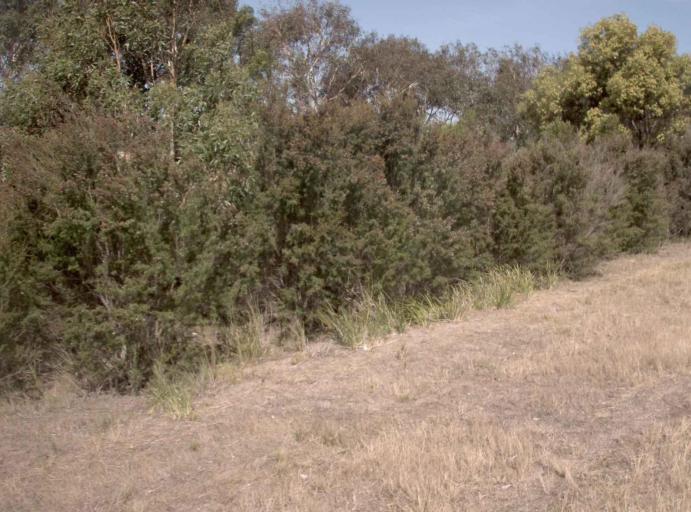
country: AU
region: Victoria
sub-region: Wellington
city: Sale
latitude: -38.3400
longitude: 147.1657
